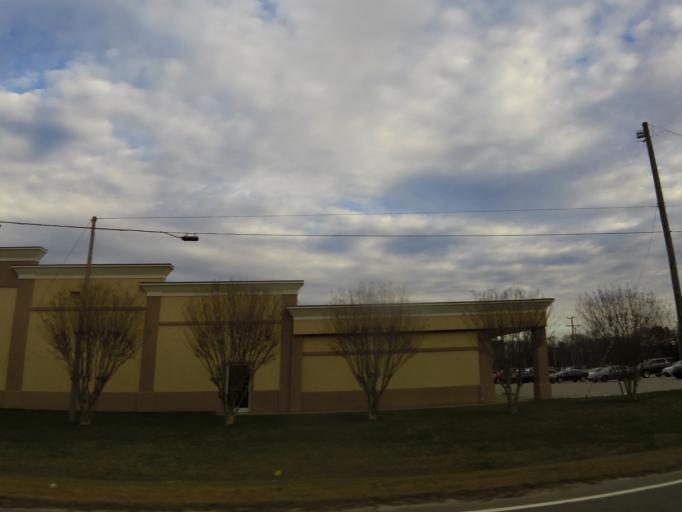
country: US
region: North Carolina
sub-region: Nash County
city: Rocky Mount
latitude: 35.9882
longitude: -77.7825
